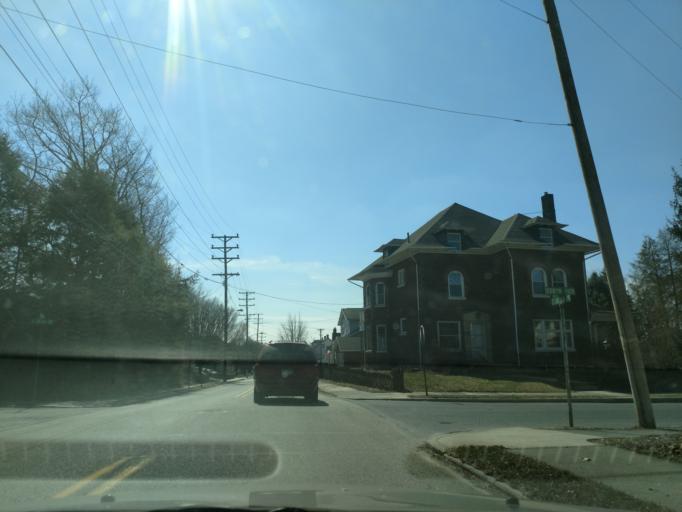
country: US
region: Pennsylvania
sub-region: Lebanon County
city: Lebanon
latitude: 40.3369
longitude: -76.4119
